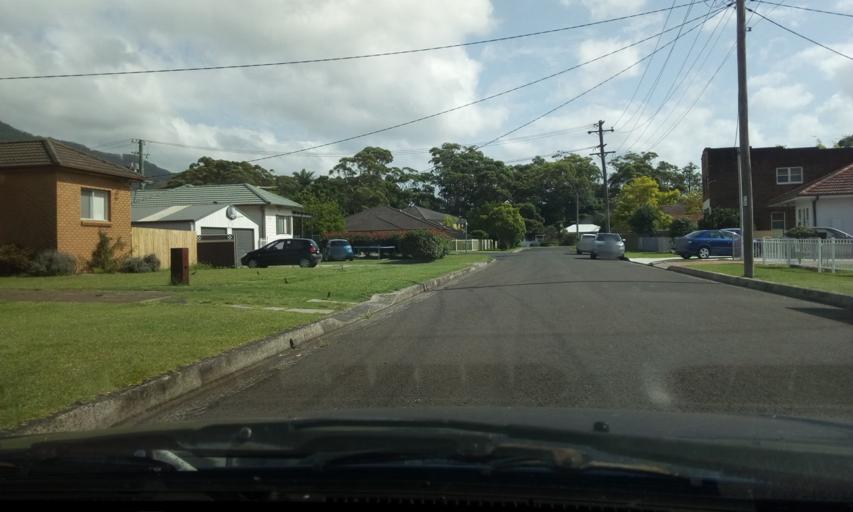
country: AU
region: New South Wales
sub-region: Wollongong
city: Corrimal
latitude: -34.3799
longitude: 150.8932
